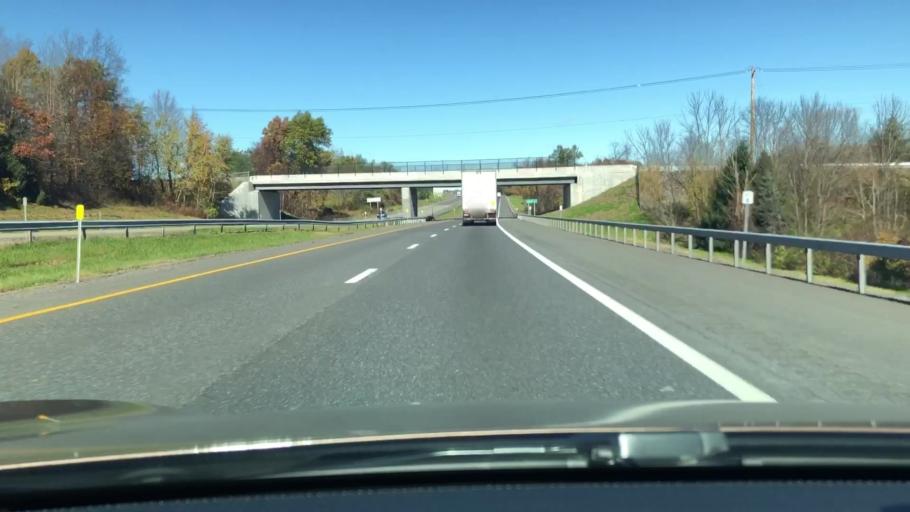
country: US
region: New York
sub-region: Ulster County
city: Plattekill
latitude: 41.6196
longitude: -74.0811
